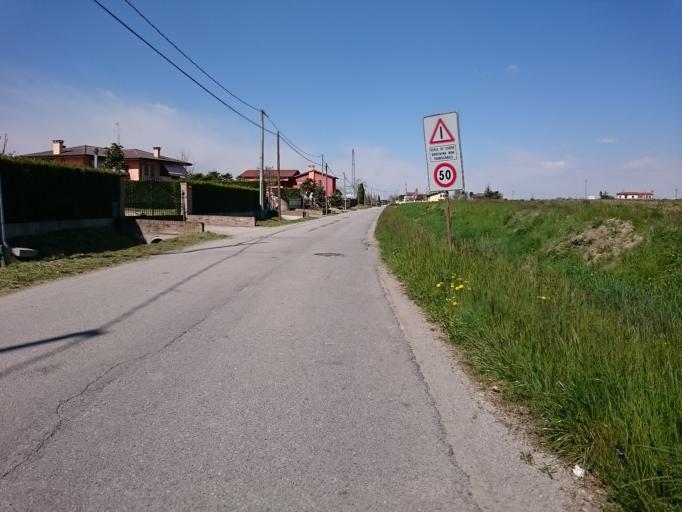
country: IT
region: Veneto
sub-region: Provincia di Padova
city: Brugine
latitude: 45.3006
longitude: 11.9850
